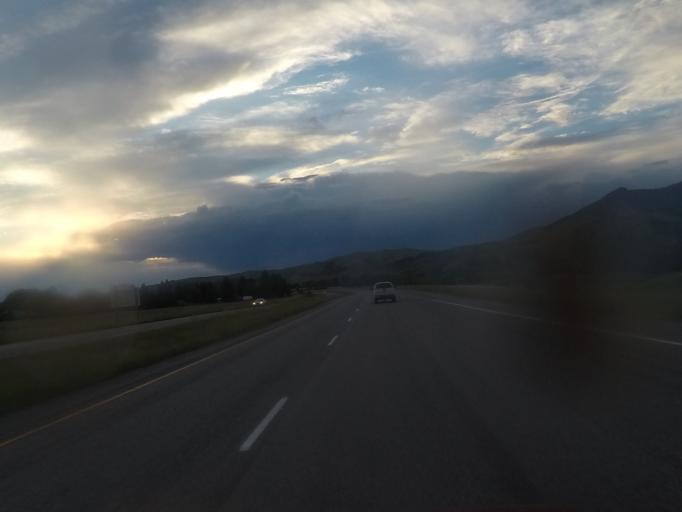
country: US
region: Montana
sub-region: Gallatin County
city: Bozeman
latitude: 45.6561
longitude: -110.9470
